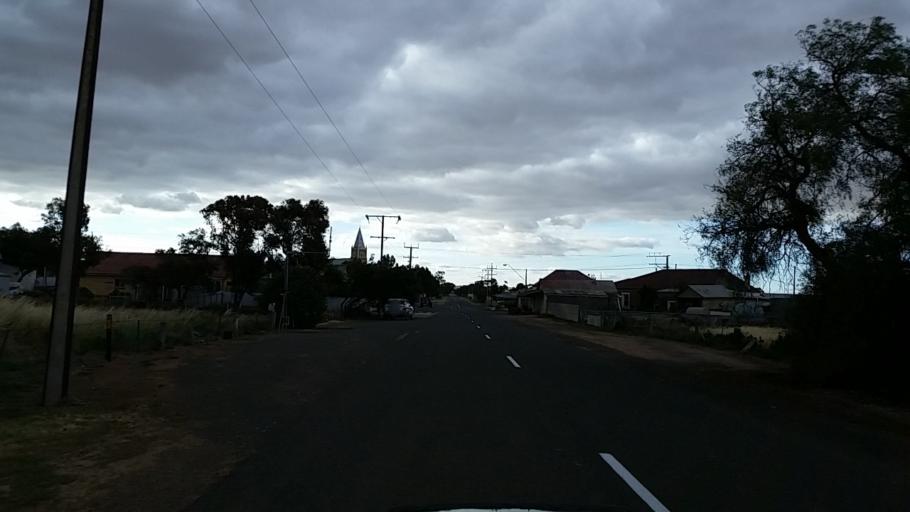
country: AU
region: South Australia
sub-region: Barossa
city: Angaston
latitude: -34.5739
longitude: 139.2961
